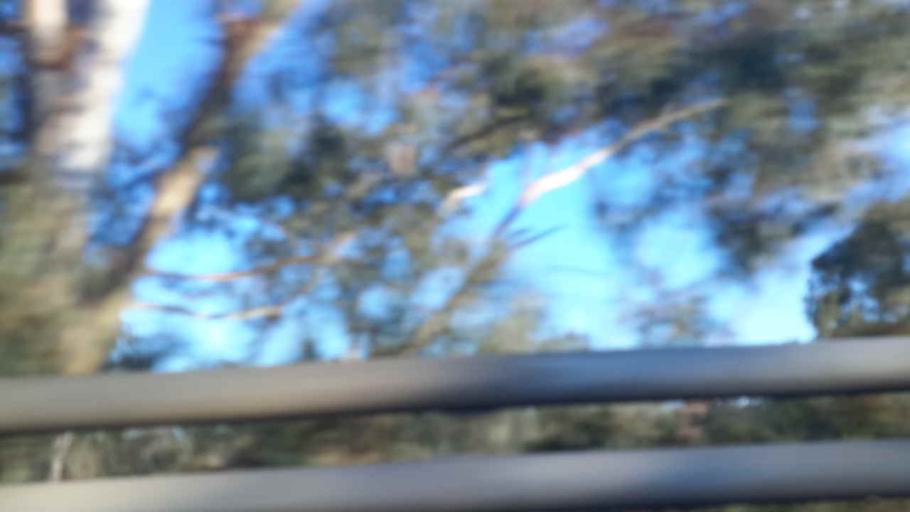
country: AU
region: New South Wales
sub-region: Camden
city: Camden South
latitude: -34.0714
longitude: 150.7001
